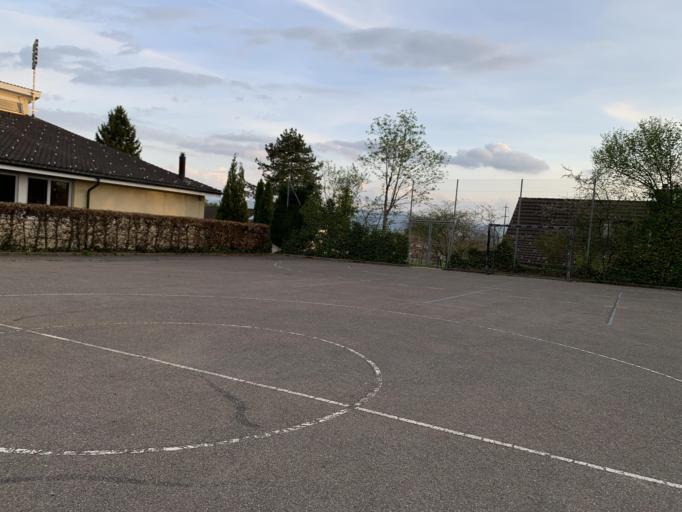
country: CH
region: Zurich
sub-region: Bezirk Hinwil
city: Hadlikon
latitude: 47.2886
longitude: 8.8522
